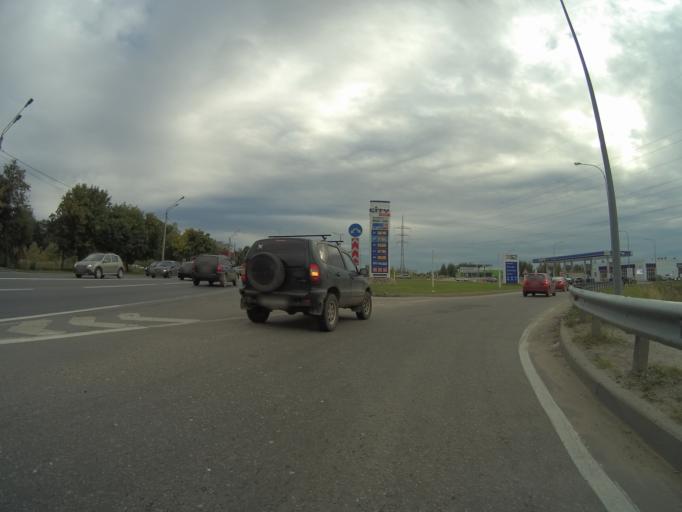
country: RU
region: Vladimir
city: Vladimir
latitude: 56.1348
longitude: 40.3504
